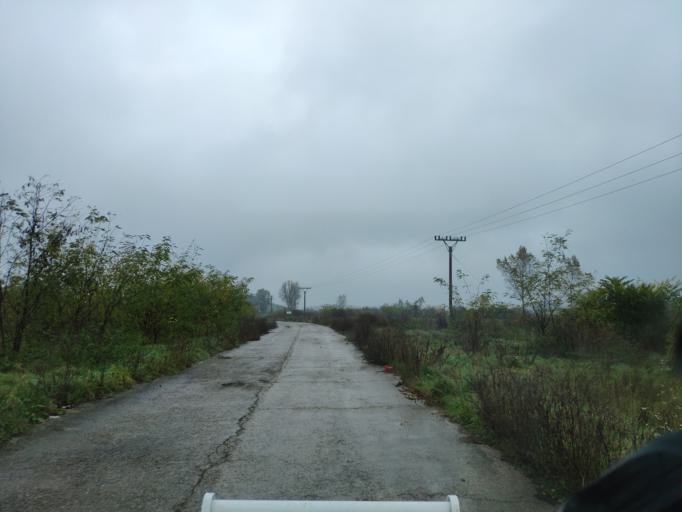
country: SK
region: Kosicky
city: Cierna nad Tisou
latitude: 48.4389
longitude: 22.0009
